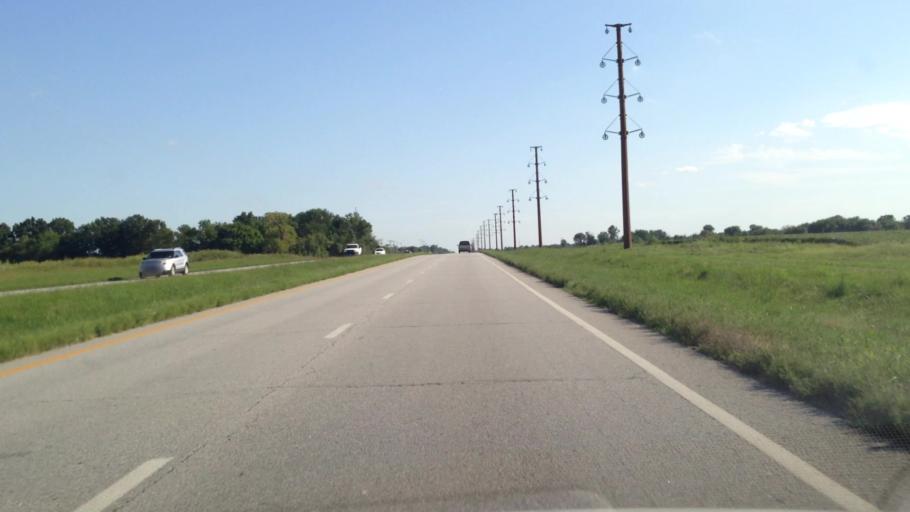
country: US
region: Kansas
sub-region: Crawford County
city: Frontenac
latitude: 37.4957
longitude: -94.7053
